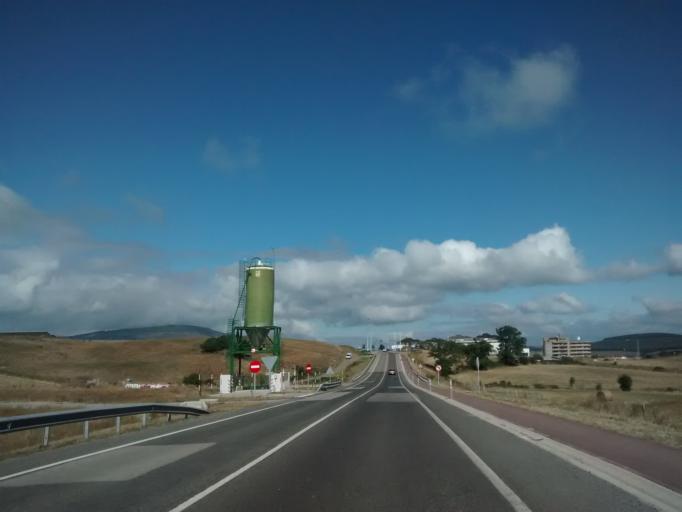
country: ES
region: Cantabria
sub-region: Provincia de Cantabria
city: Reinosa
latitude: 43.0070
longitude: -4.1375
